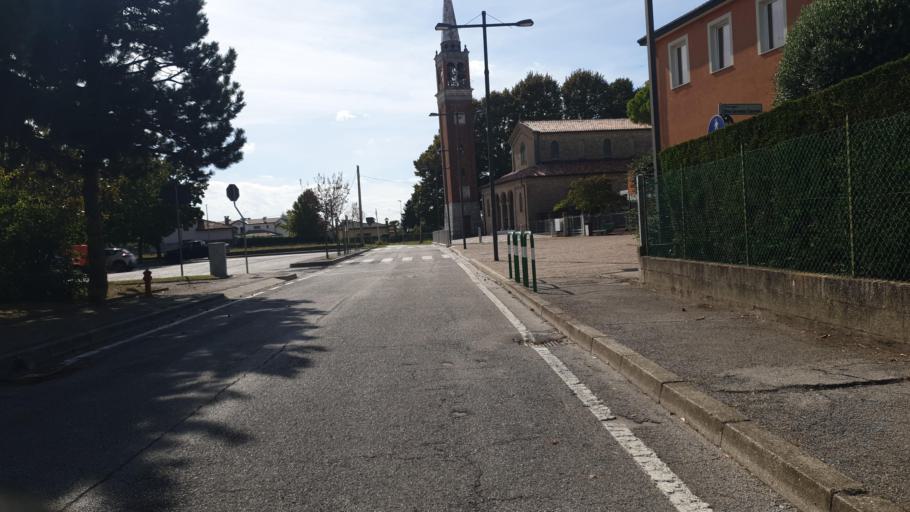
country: IT
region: Veneto
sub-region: Provincia di Padova
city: Arzergrande
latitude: 45.2852
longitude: 12.0568
